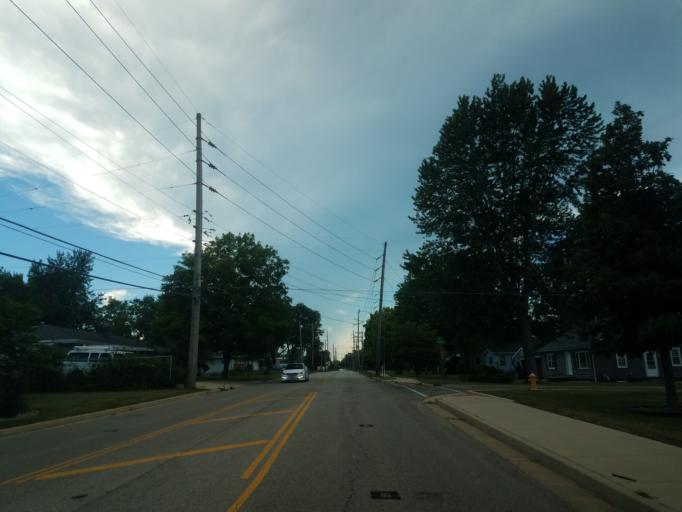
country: US
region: Illinois
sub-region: McLean County
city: Bloomington
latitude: 40.4635
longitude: -88.9766
